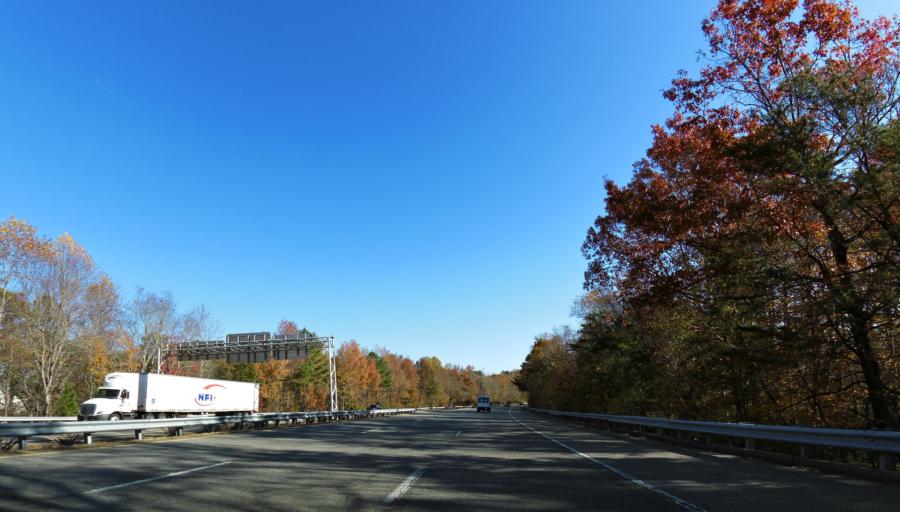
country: US
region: Virginia
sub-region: City of Williamsburg
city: Williamsburg
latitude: 37.2533
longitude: -76.6595
